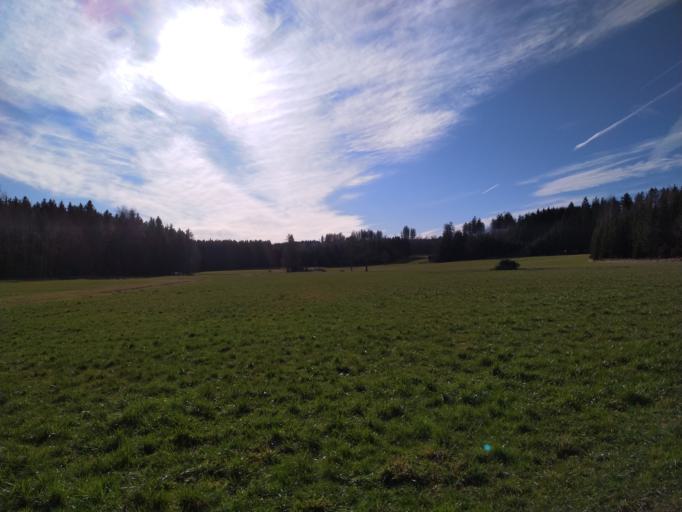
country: DE
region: Bavaria
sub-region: Swabia
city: Bad Worishofen
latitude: 47.9929
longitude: 10.5782
